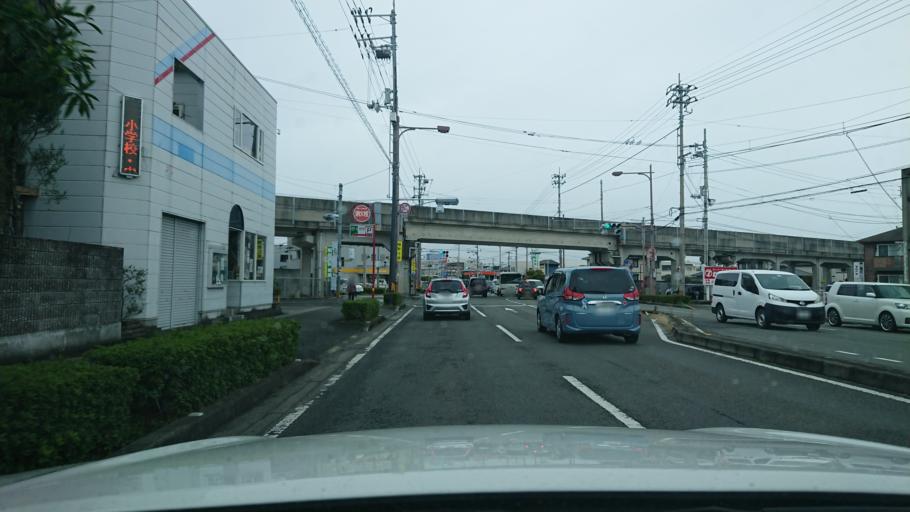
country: JP
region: Tokushima
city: Tokushima-shi
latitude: 34.0862
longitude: 134.5310
